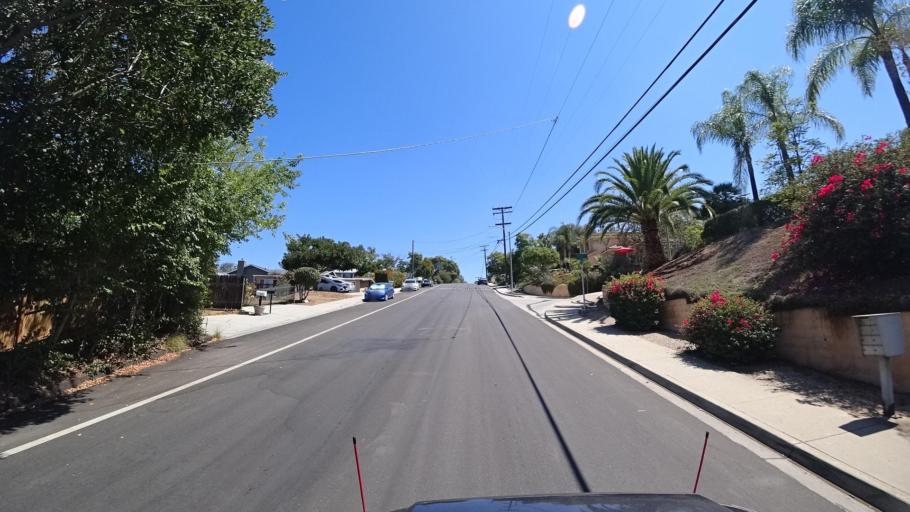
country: US
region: California
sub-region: San Diego County
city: Fallbrook
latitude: 33.3893
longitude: -117.2468
